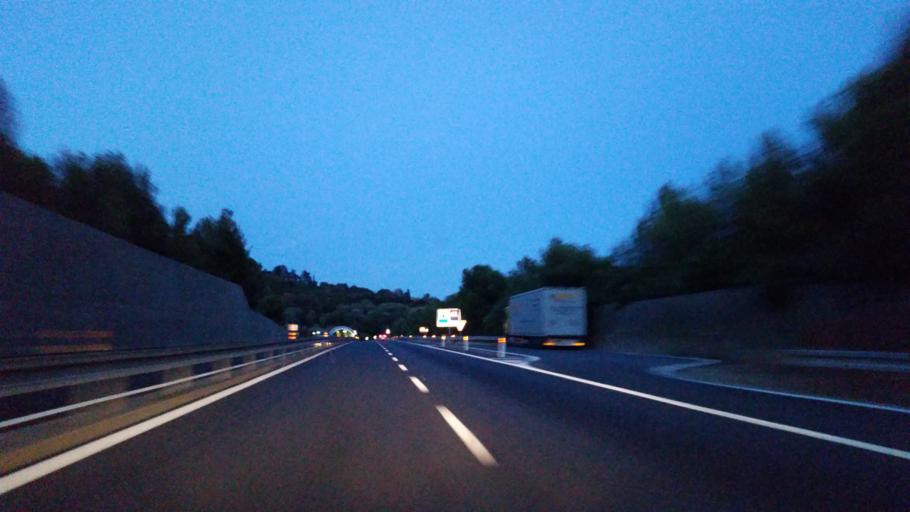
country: IT
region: Liguria
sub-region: Provincia di Imperia
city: Imperia
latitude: 43.8893
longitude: 8.0209
